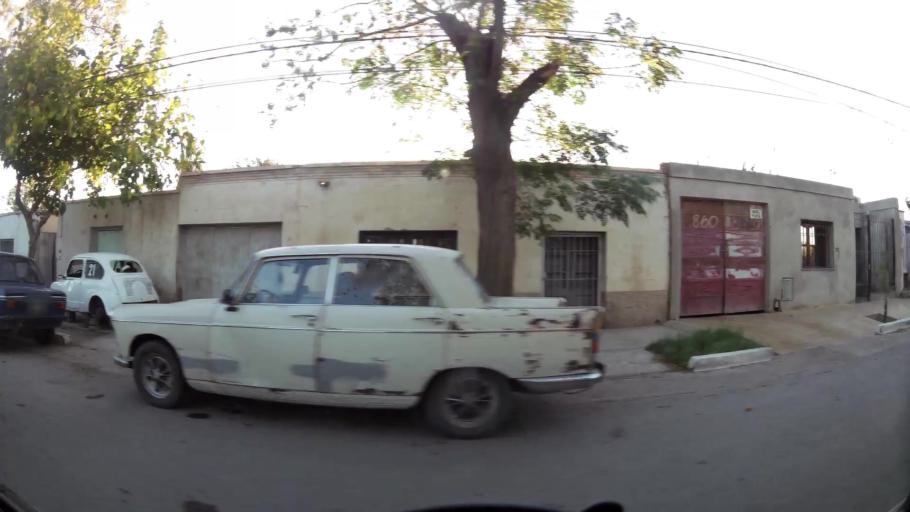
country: AR
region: San Juan
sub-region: Departamento de Santa Lucia
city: Santa Lucia
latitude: -31.5223
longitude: -68.5078
